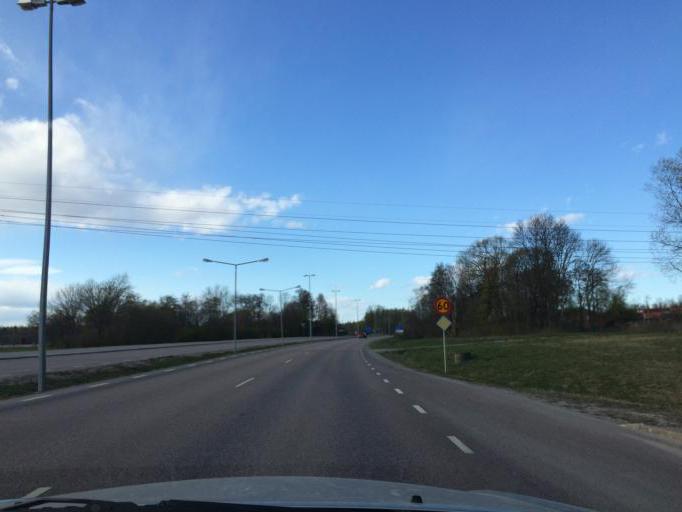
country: SE
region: Vaestmanland
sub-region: Vasteras
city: Vasteras
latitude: 59.6326
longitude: 16.5320
